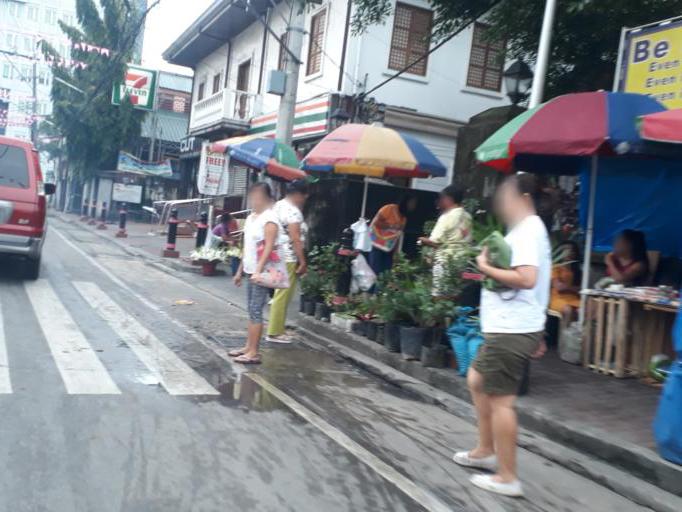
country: PH
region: Metro Manila
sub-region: Caloocan City
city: Niugan
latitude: 14.6583
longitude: 120.9519
